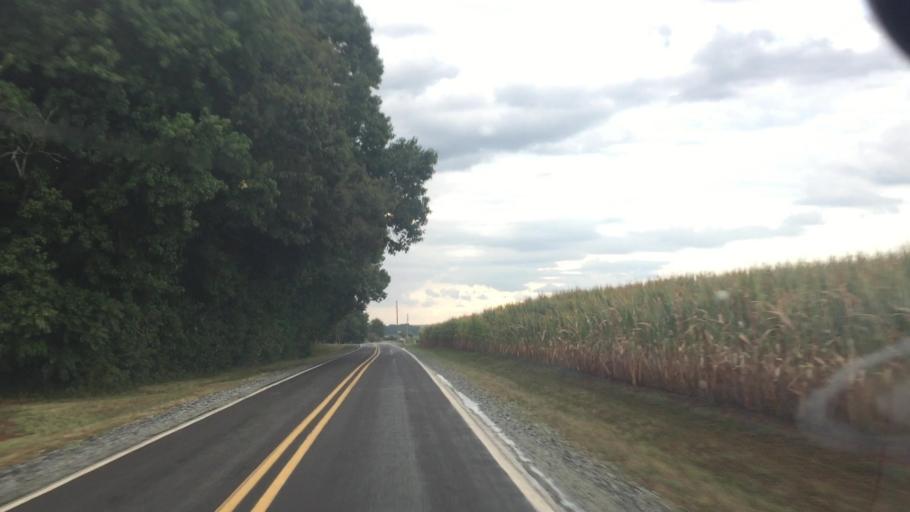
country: US
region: North Carolina
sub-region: Rowan County
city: China Grove
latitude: 35.6472
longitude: -80.6648
